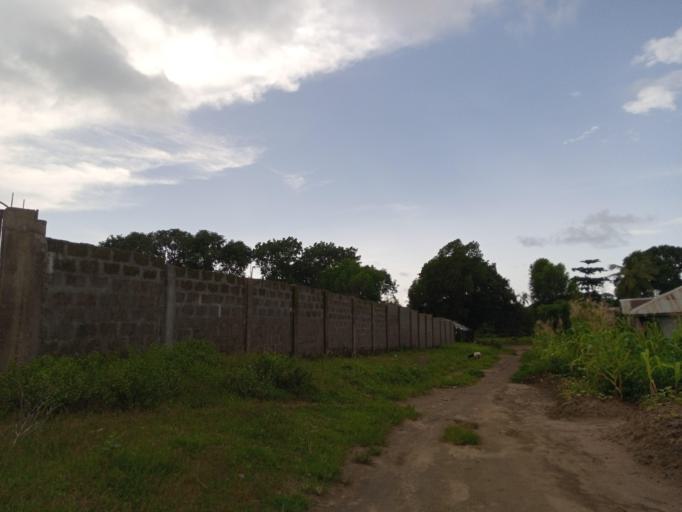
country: SL
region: Northern Province
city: Masoyila
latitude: 8.6005
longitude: -13.2031
